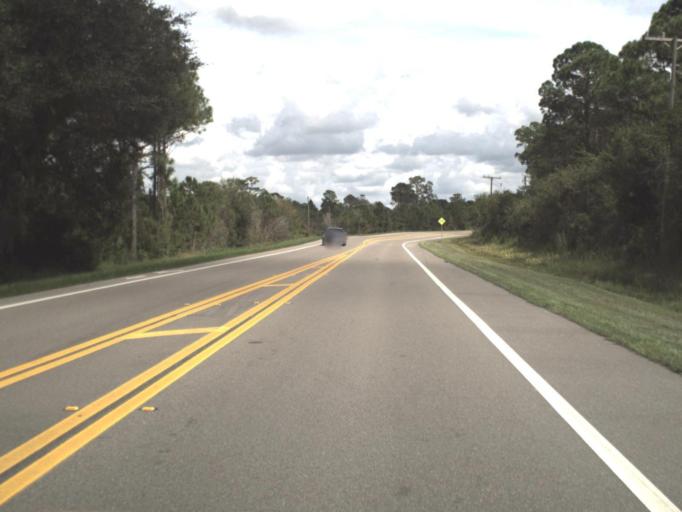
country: US
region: Florida
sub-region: Sarasota County
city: Lake Sarasota
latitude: 27.2461
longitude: -82.3600
